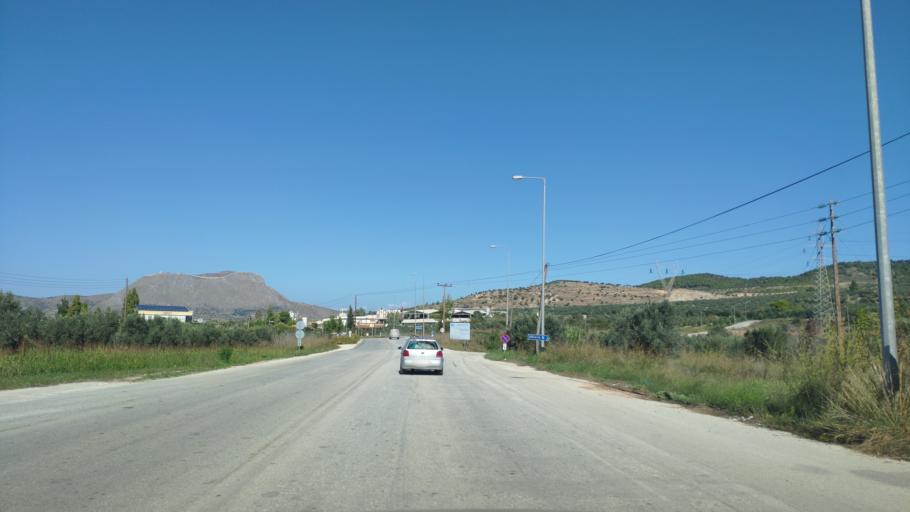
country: GR
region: Peloponnese
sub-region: Nomos Korinthias
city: Athikia
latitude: 37.8470
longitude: 22.8983
